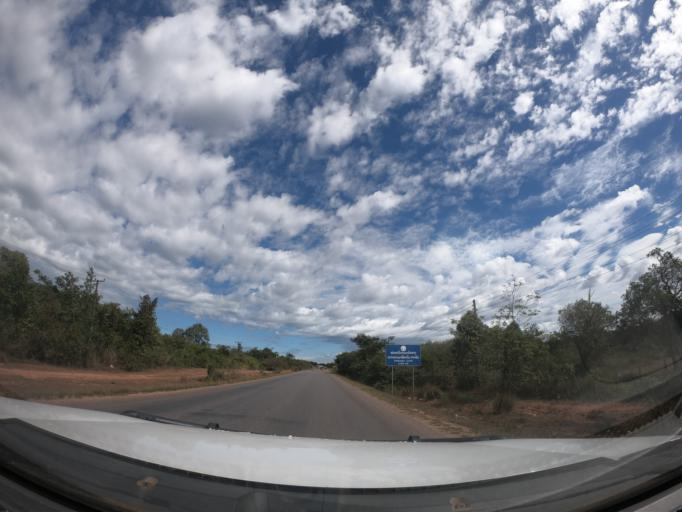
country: LA
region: Bolikhamxai
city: Muang Pakxan
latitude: 18.4351
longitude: 103.5470
